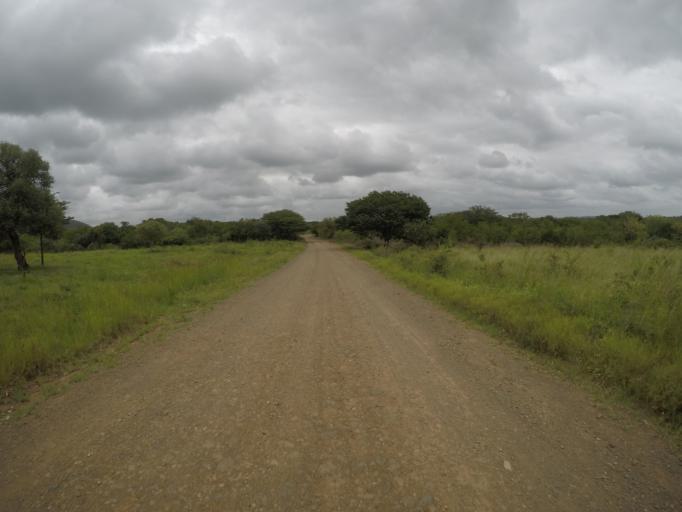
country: ZA
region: KwaZulu-Natal
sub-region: uThungulu District Municipality
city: Empangeni
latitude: -28.5624
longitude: 31.8733
